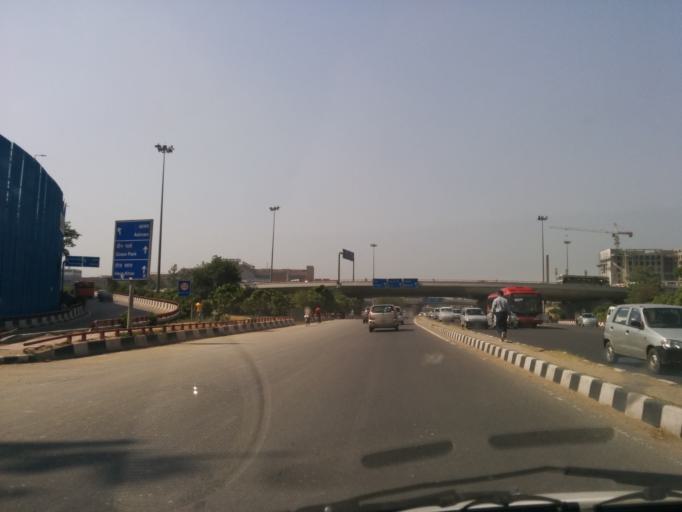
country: IN
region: NCT
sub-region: New Delhi
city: New Delhi
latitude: 28.5720
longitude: 77.2092
